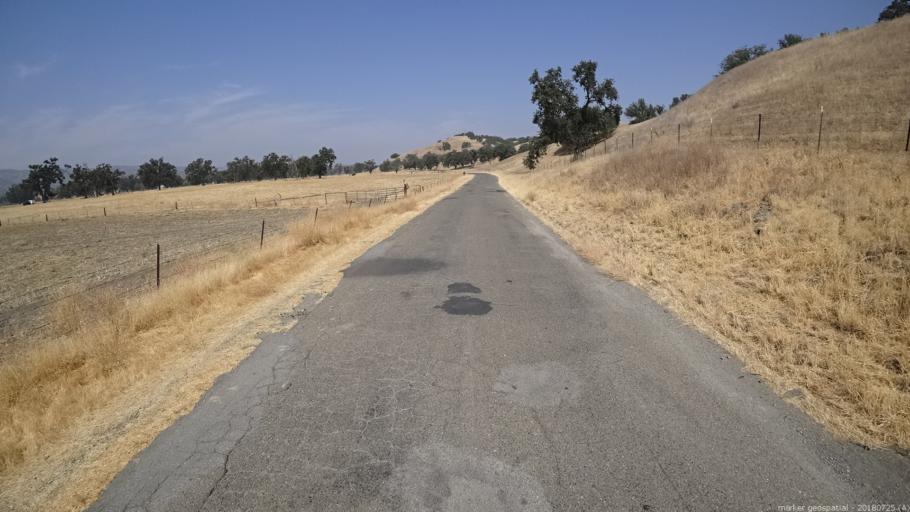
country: US
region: California
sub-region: San Luis Obispo County
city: Shandon
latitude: 35.8838
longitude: -120.4253
